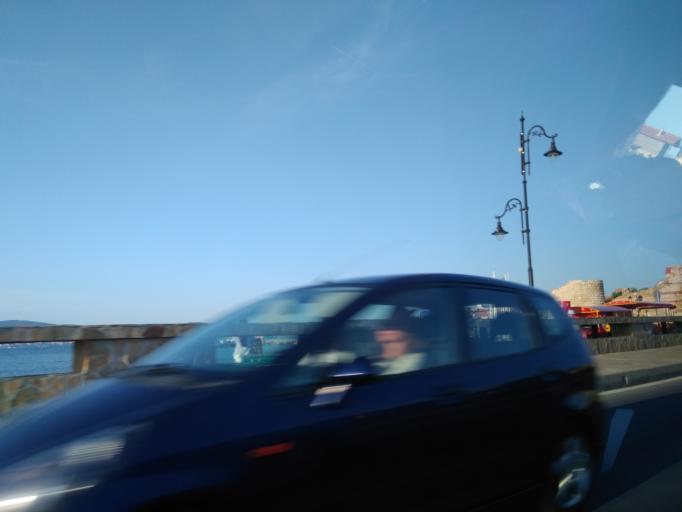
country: BG
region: Burgas
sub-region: Obshtina Nesebur
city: Nesebar
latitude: 42.6591
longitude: 27.7295
